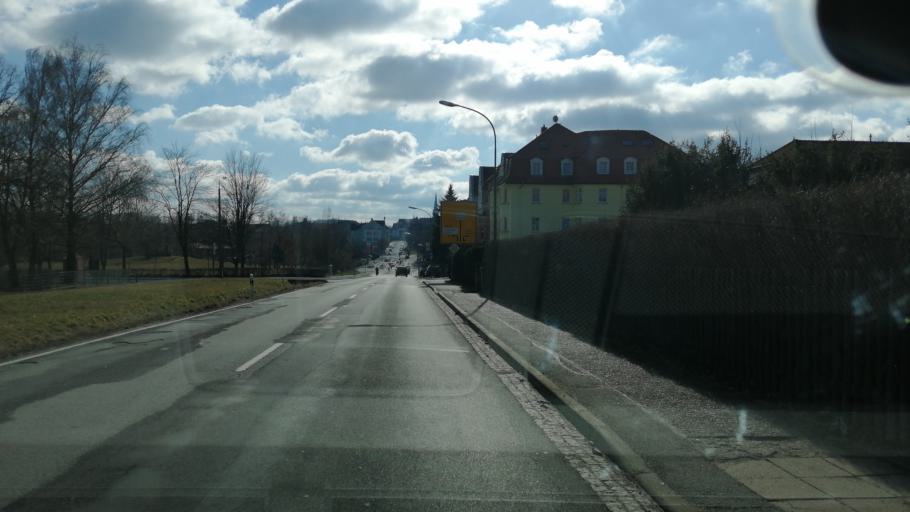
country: DE
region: Saxony
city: Lobau
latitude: 51.1060
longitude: 14.6705
